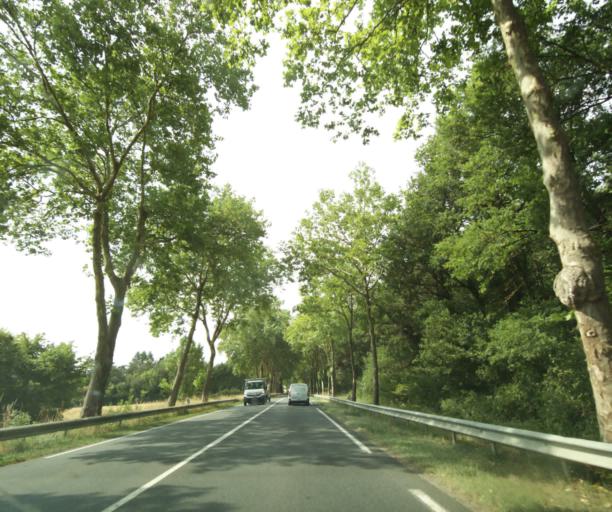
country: FR
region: Centre
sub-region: Departement d'Indre-et-Loire
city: Charentilly
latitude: 47.4710
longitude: 0.6172
